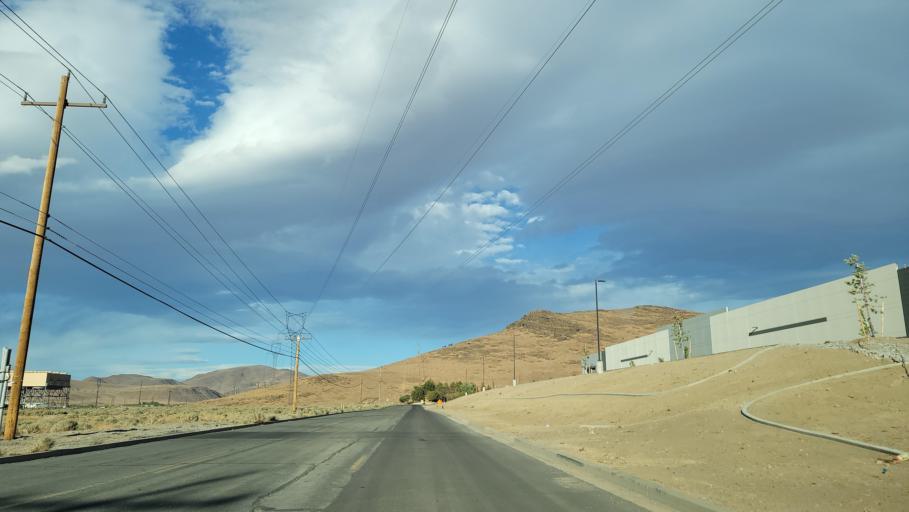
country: US
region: Nevada
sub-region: Washoe County
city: Spanish Springs
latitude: 39.5576
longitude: -119.5302
